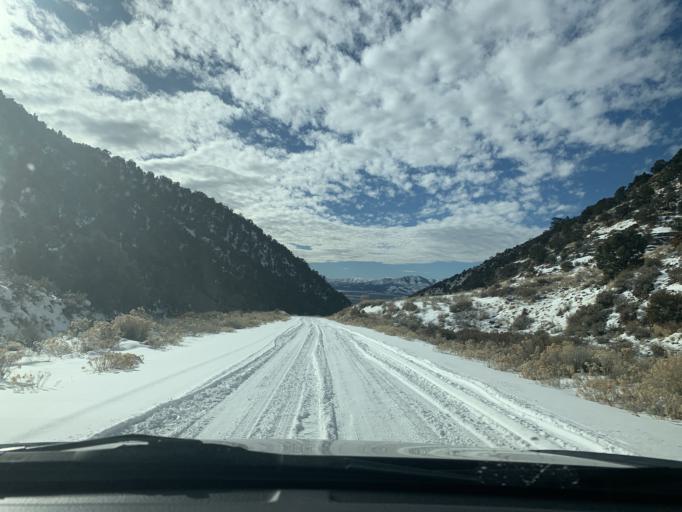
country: US
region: Utah
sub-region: Utah County
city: Eagle Mountain
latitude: 40.3156
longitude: -112.2311
